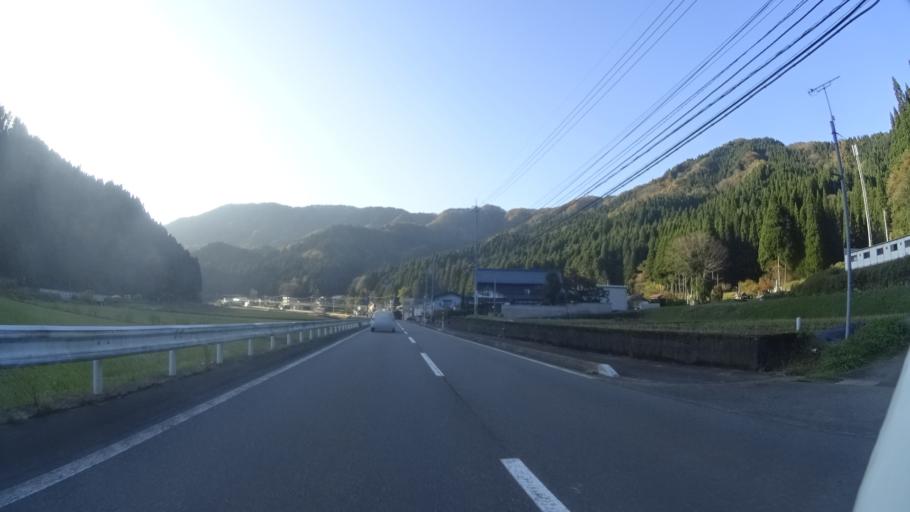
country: JP
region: Fukui
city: Ono
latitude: 36.0083
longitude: 136.3944
